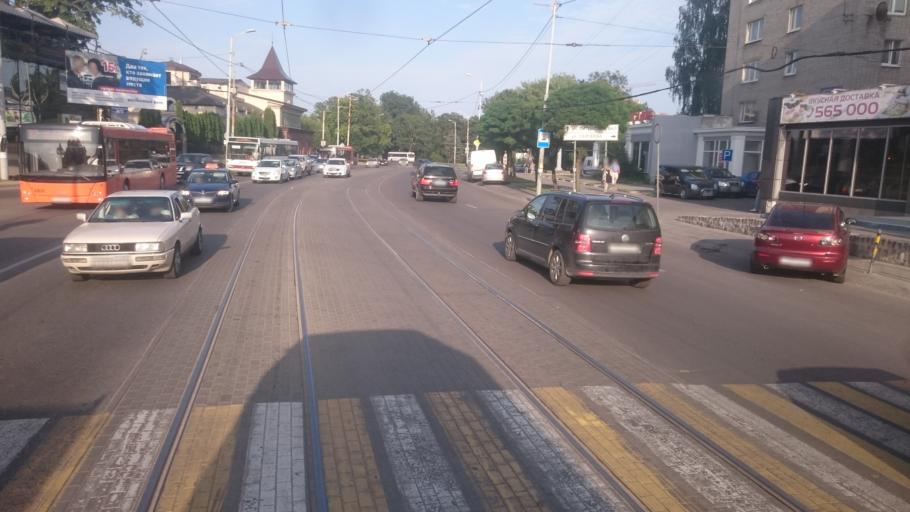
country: RU
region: Kaliningrad
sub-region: Gorod Kaliningrad
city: Kaliningrad
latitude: 54.7207
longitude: 20.5167
